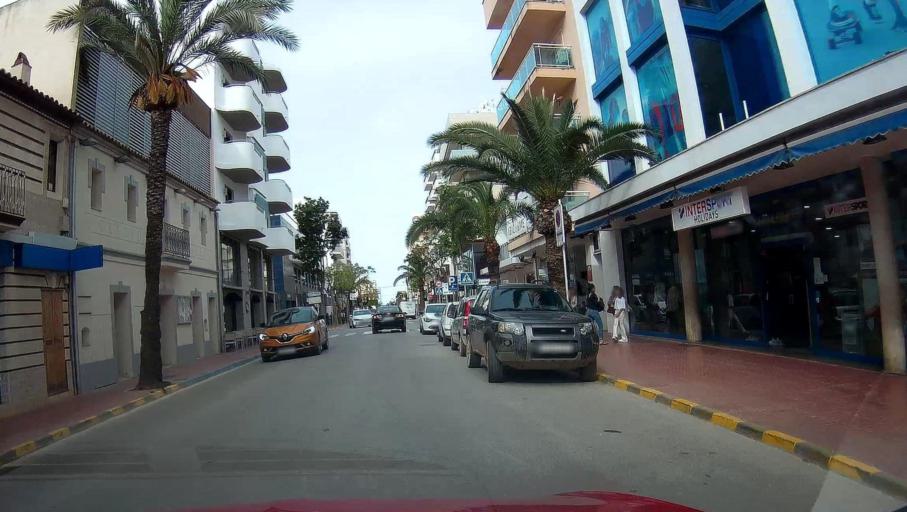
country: ES
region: Balearic Islands
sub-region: Illes Balears
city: Santa Eularia des Riu
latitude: 38.9857
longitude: 1.5357
